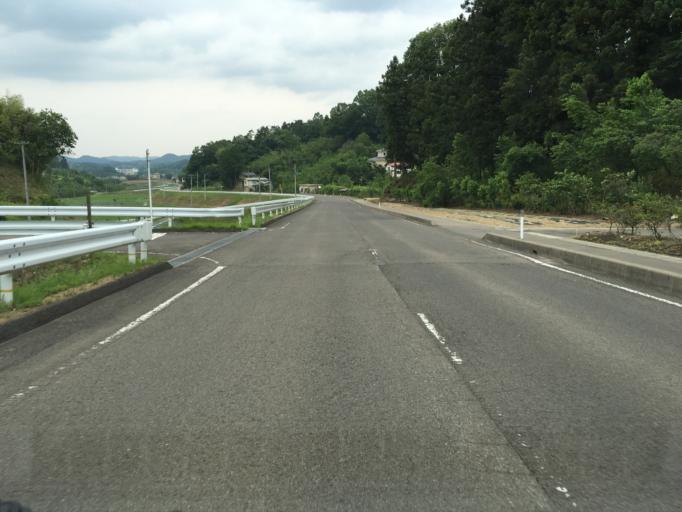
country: JP
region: Fukushima
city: Nihommatsu
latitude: 37.6427
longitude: 140.5356
